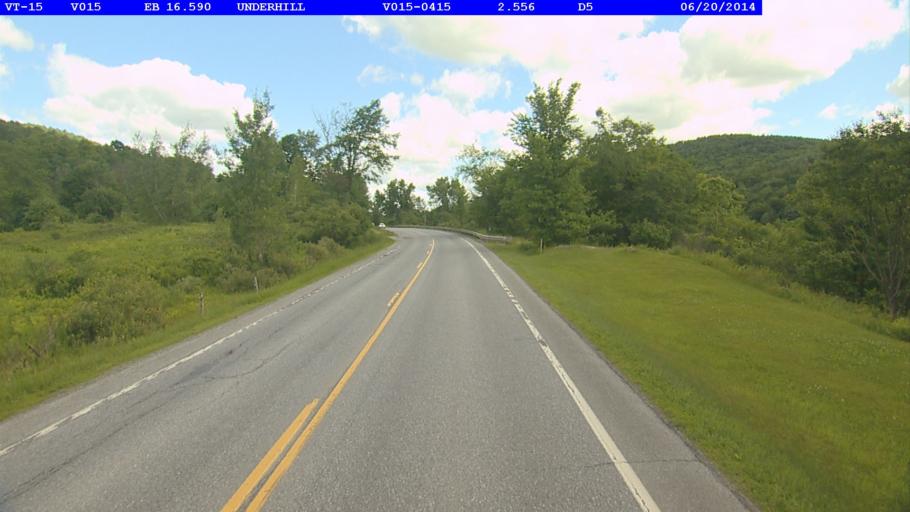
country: US
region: Vermont
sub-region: Chittenden County
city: Jericho
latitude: 44.5606
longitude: -72.9426
